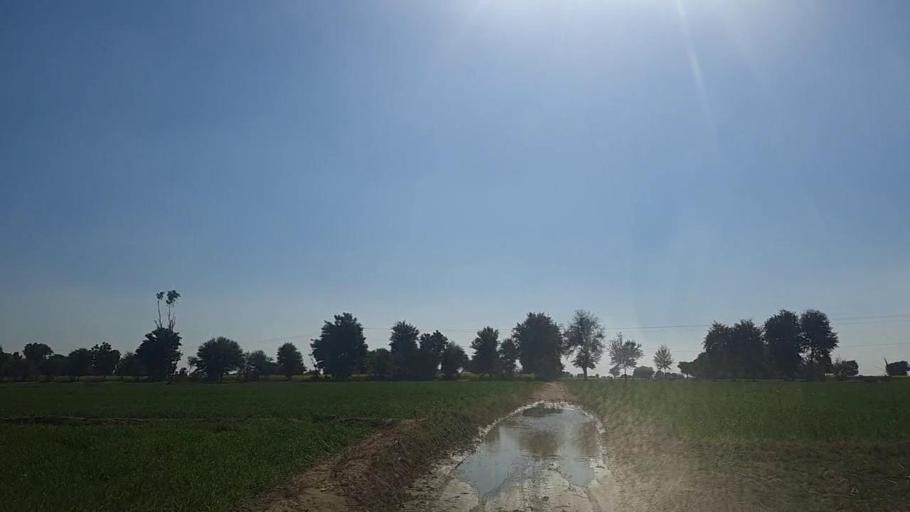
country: PK
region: Sindh
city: Khadro
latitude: 26.1583
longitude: 68.8278
